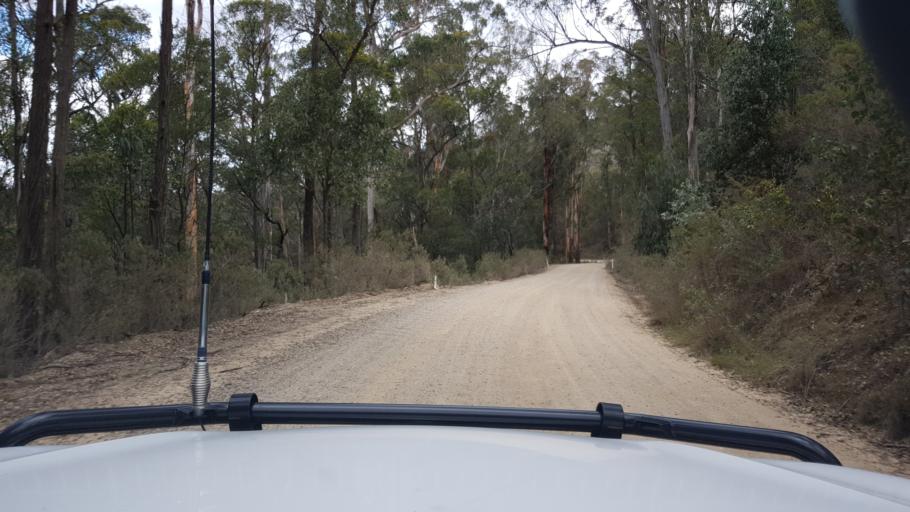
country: AU
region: Victoria
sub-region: East Gippsland
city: Bairnsdale
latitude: -37.6910
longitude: 147.5643
